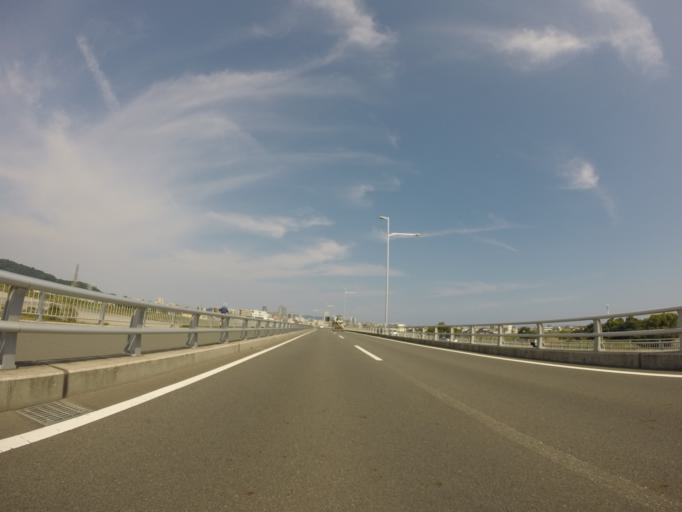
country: JP
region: Shizuoka
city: Shizuoka-shi
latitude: 34.9763
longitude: 138.3594
